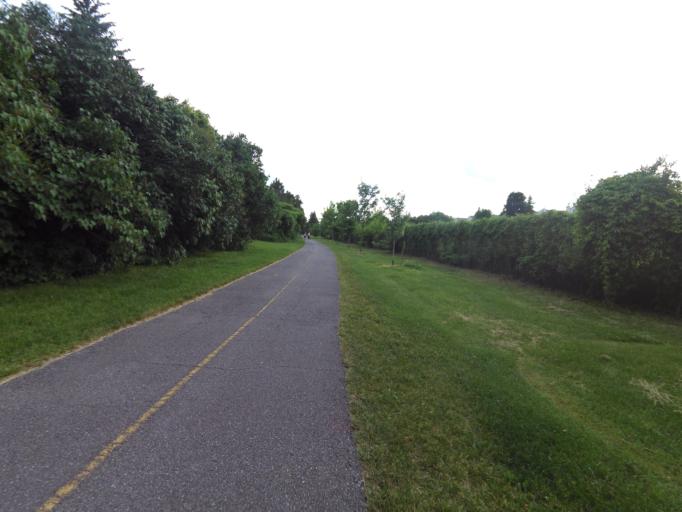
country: CA
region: Ontario
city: Bells Corners
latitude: 45.2645
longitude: -75.7665
